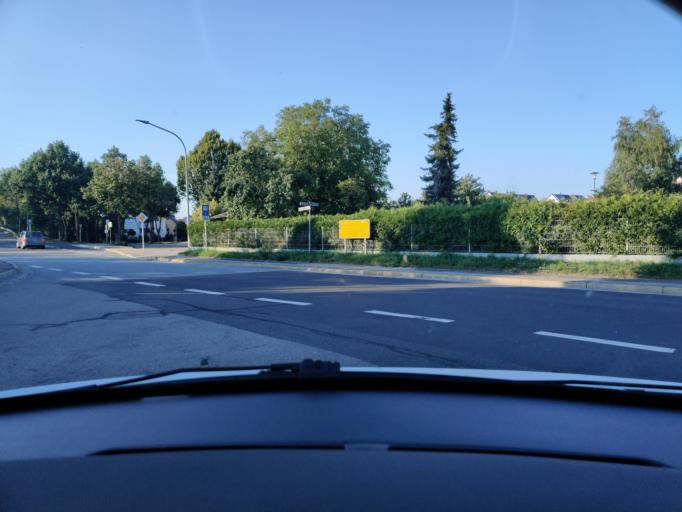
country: DE
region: Bavaria
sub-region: Upper Palatinate
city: Nabburg
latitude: 49.4494
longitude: 12.1940
